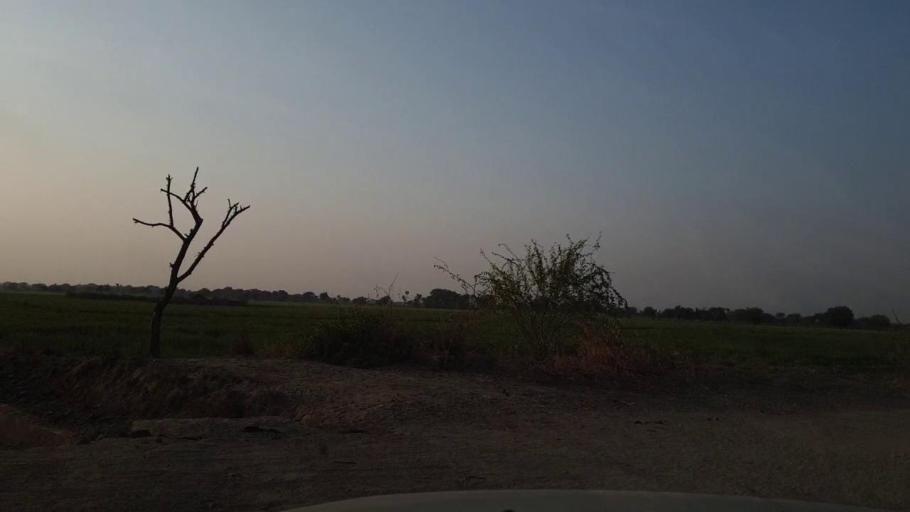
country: PK
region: Sindh
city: Pithoro
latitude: 25.6537
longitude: 69.2127
